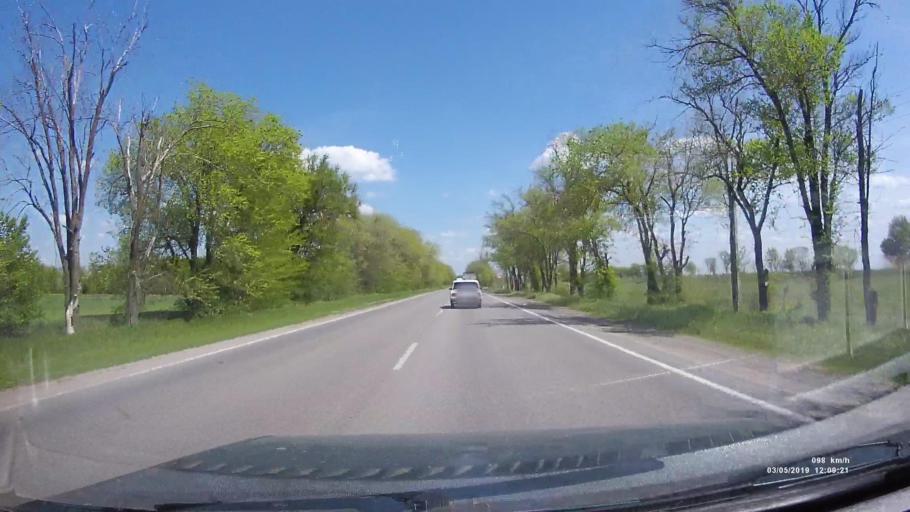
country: RU
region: Rostov
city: Bagayevskaya
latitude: 47.2942
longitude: 40.5147
